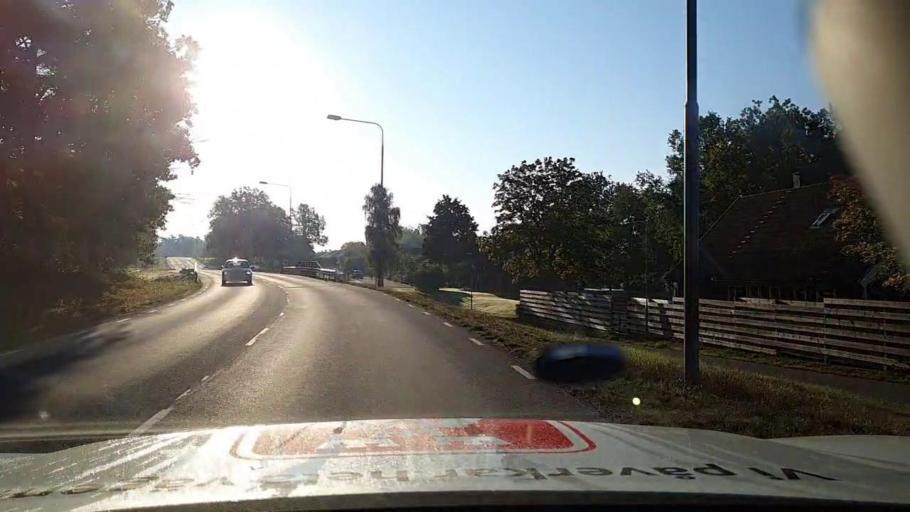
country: SE
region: Kalmar
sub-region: Vasterviks Kommun
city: Vaestervik
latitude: 57.7540
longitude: 16.6080
